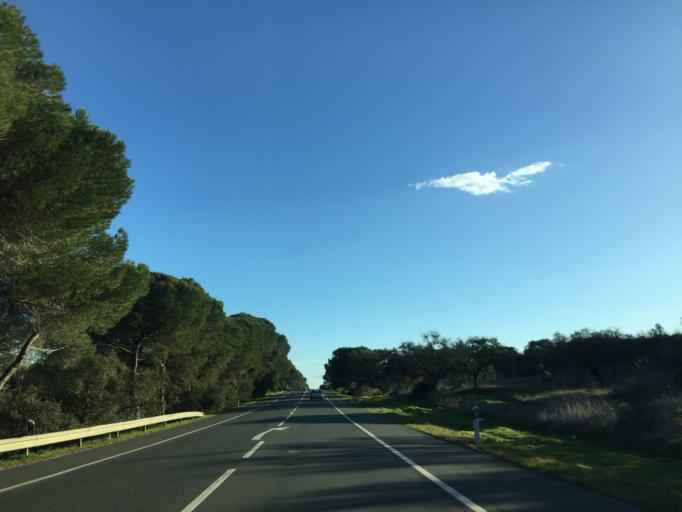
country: PT
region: Setubal
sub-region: Grandola
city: Grandola
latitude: 38.0881
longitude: -8.4179
